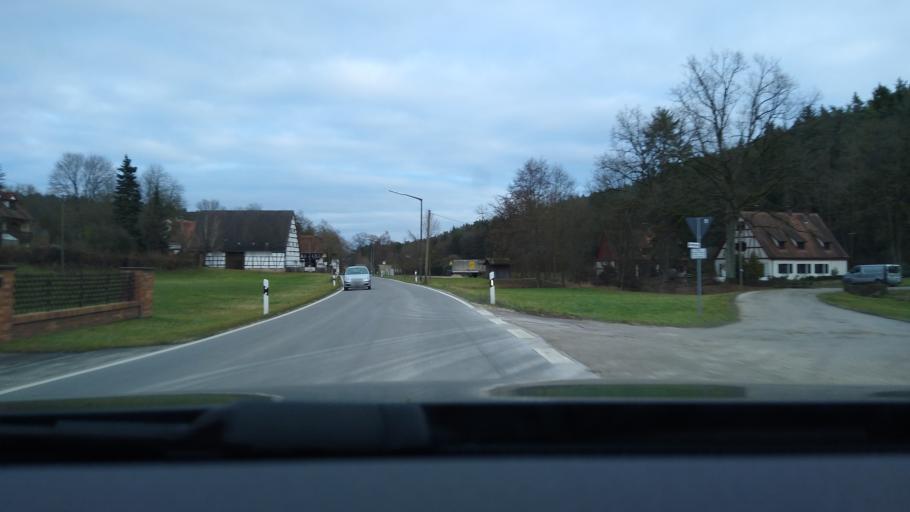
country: DE
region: Bavaria
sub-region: Regierungsbezirk Mittelfranken
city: Oberasbach
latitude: 49.3694
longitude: 10.9788
